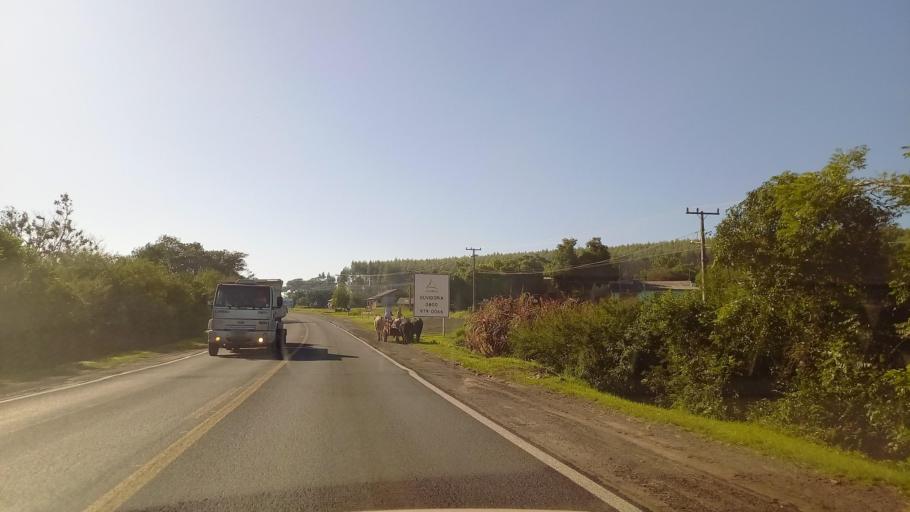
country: BR
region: Rio Grande do Sul
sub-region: Taquari
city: Taquari
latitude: -29.7111
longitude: -51.7697
